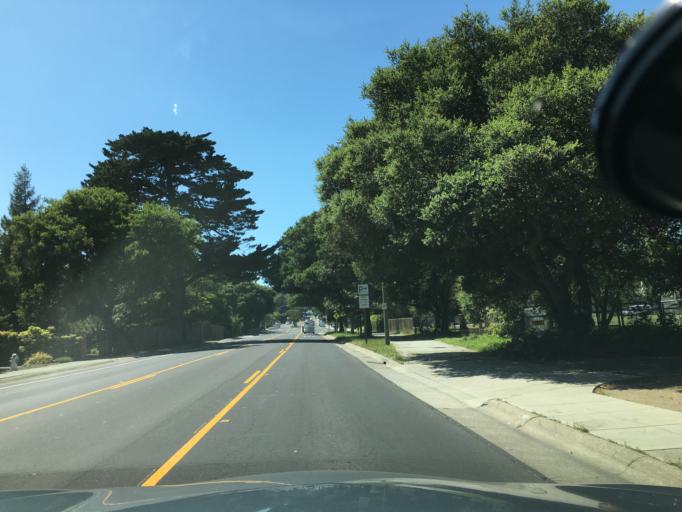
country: US
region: California
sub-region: San Mateo County
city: Belmont
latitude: 37.5132
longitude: -122.2908
